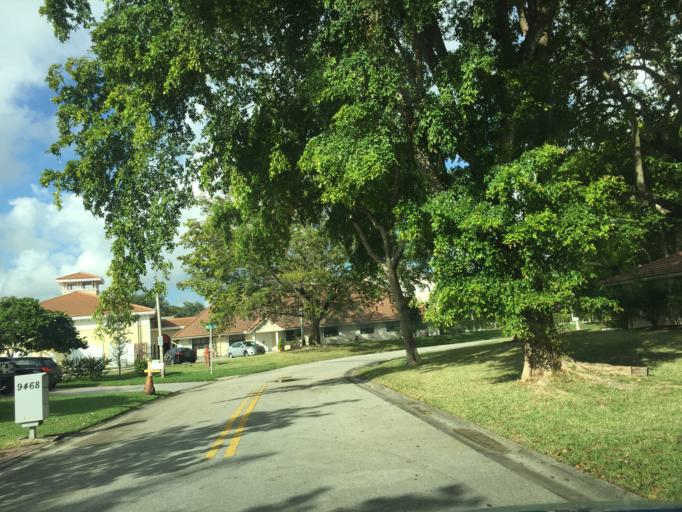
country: US
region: Florida
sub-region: Broward County
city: Tamarac
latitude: 26.2334
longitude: -80.2517
